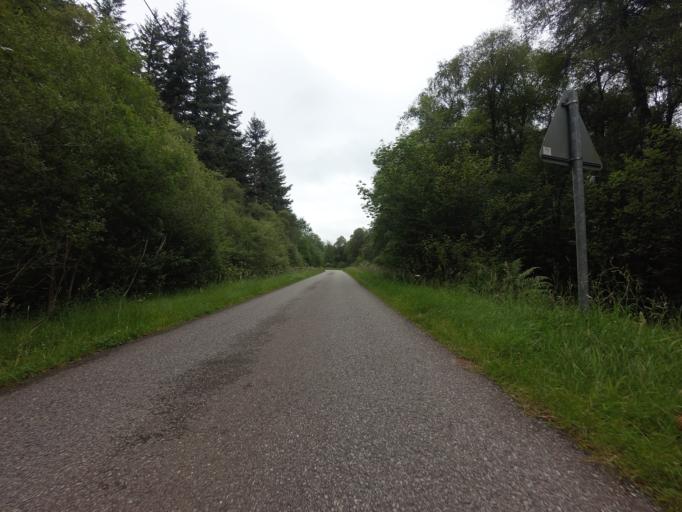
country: GB
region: Scotland
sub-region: Highland
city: Evanton
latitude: 57.9681
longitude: -4.4119
